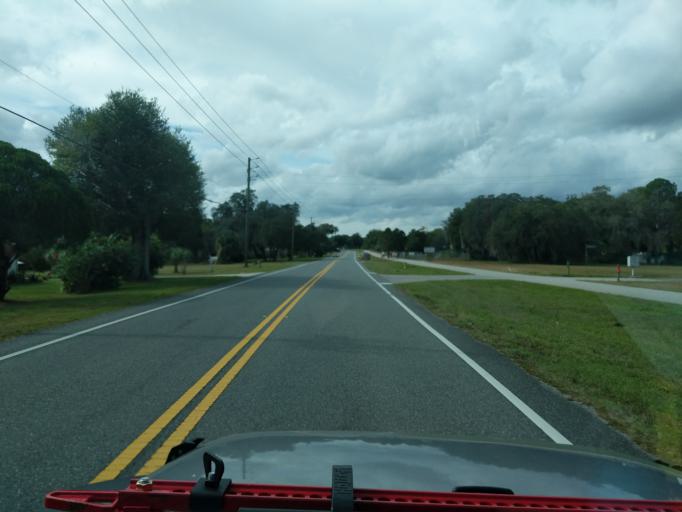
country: US
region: Florida
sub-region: Lake County
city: Clermont
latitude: 28.5754
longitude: -81.7917
